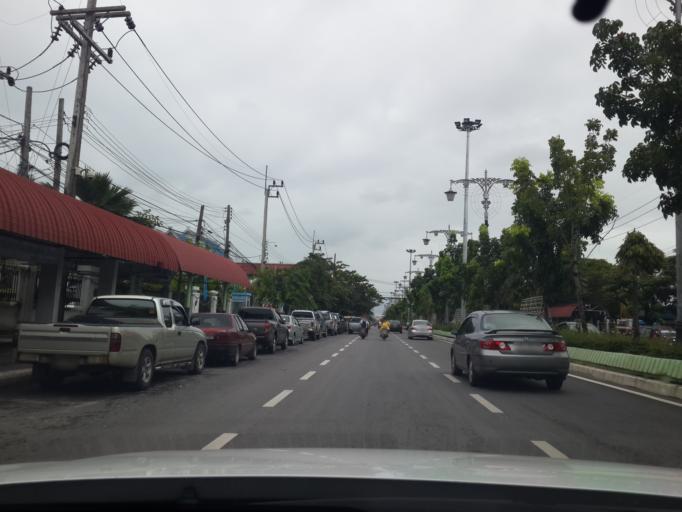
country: TH
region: Pattani
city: Pattani
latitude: 6.8693
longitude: 101.2504
